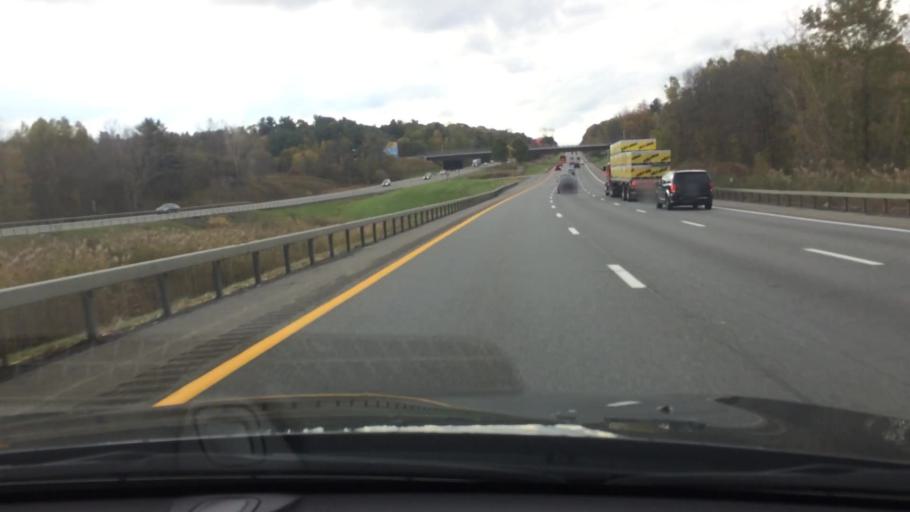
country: US
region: New York
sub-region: Saratoga County
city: Country Knolls
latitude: 42.8932
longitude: -73.7805
